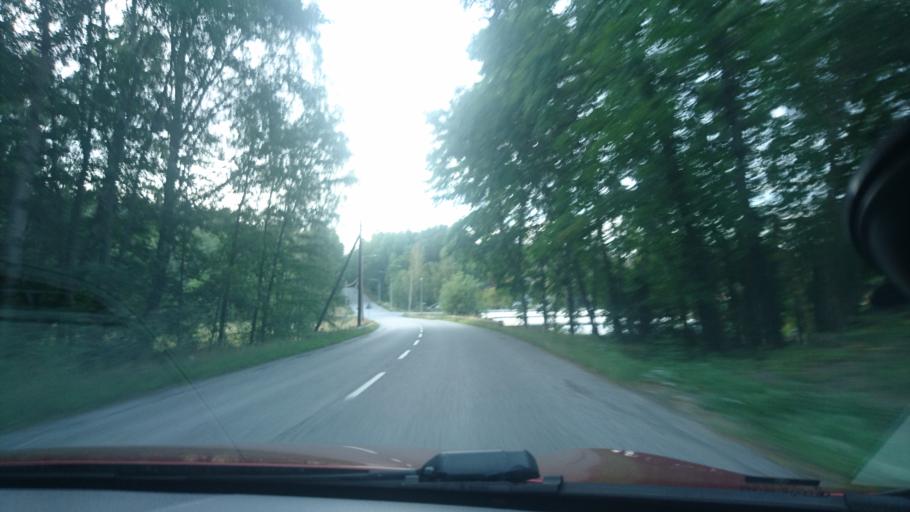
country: SE
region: Stockholm
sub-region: Sodertalje Kommun
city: Pershagen
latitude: 59.1502
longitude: 17.6514
